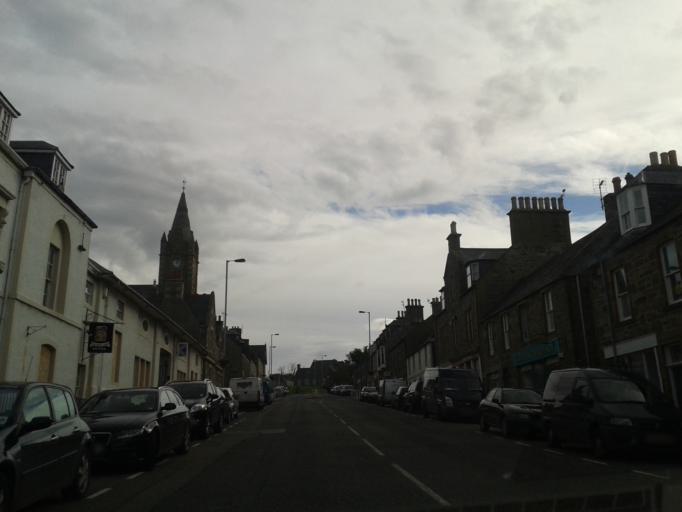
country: GB
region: Scotland
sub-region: Moray
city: Cullen
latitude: 57.6910
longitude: -2.8190
